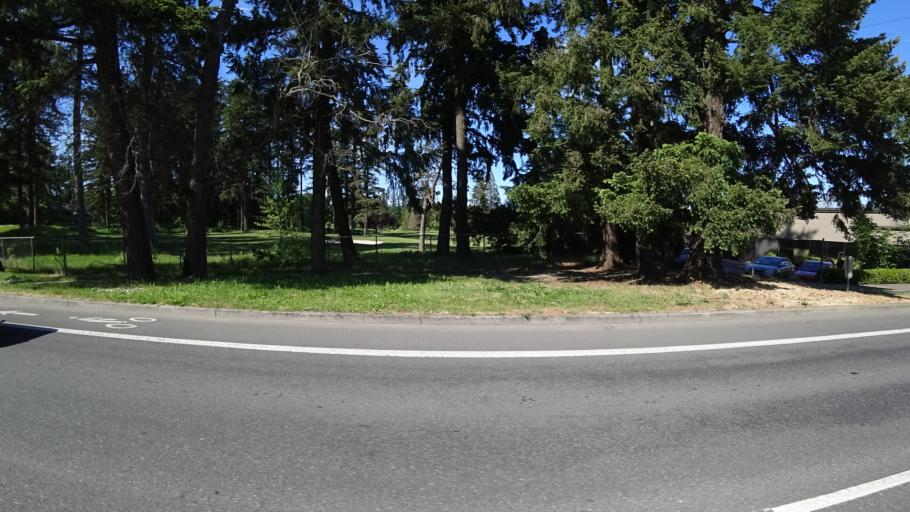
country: US
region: Oregon
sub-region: Washington County
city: Metzger
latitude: 45.4545
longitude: -122.7780
